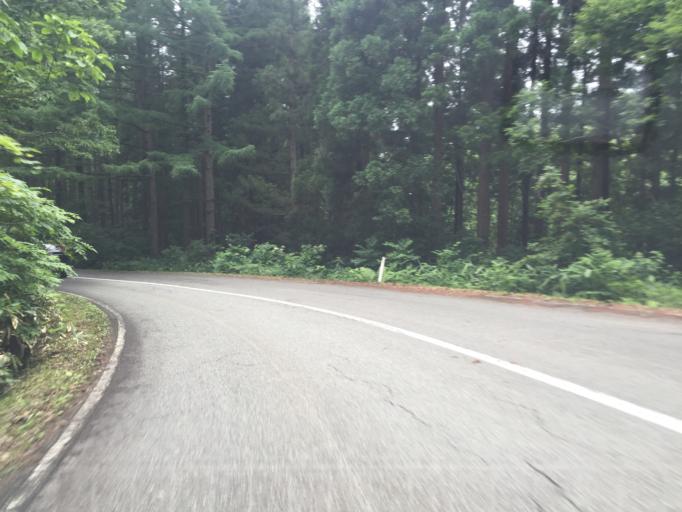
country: JP
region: Yamagata
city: Yonezawa
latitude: 37.7468
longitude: 140.0714
